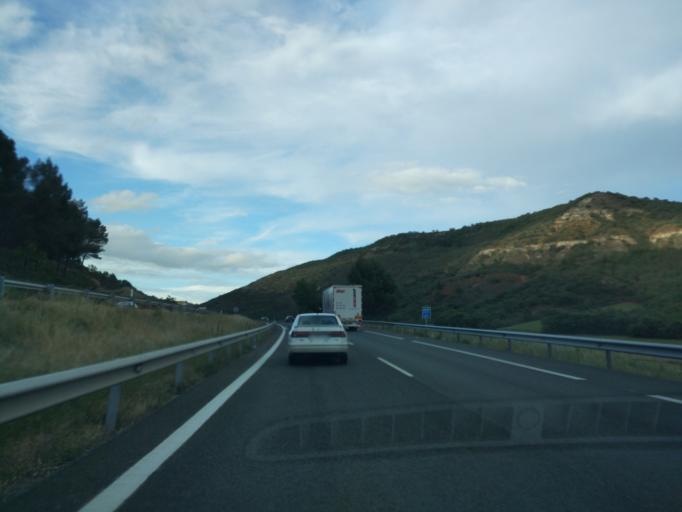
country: ES
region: Castille-La Mancha
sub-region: Provincia de Guadalajara
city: Aldeanueva de Guadalajara
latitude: 40.7039
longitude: -3.0772
